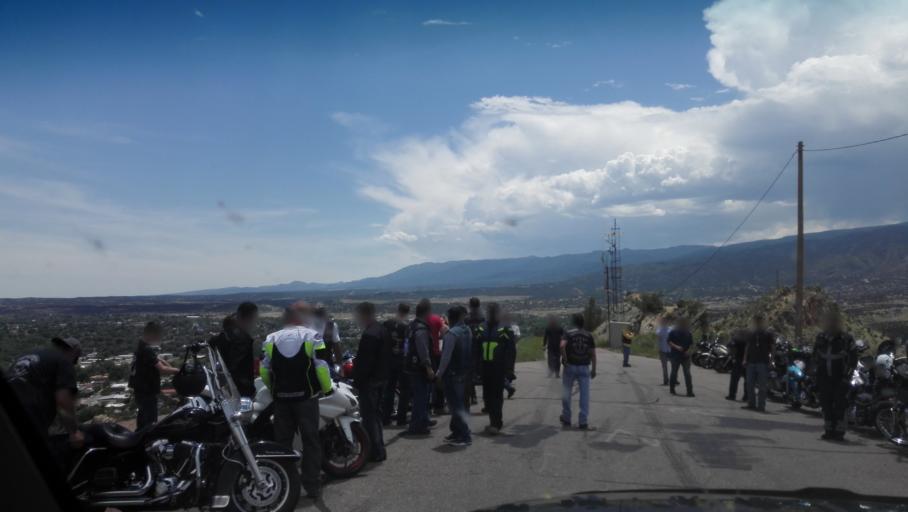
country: US
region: Colorado
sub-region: Fremont County
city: Canon City
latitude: 38.4500
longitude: -105.2492
